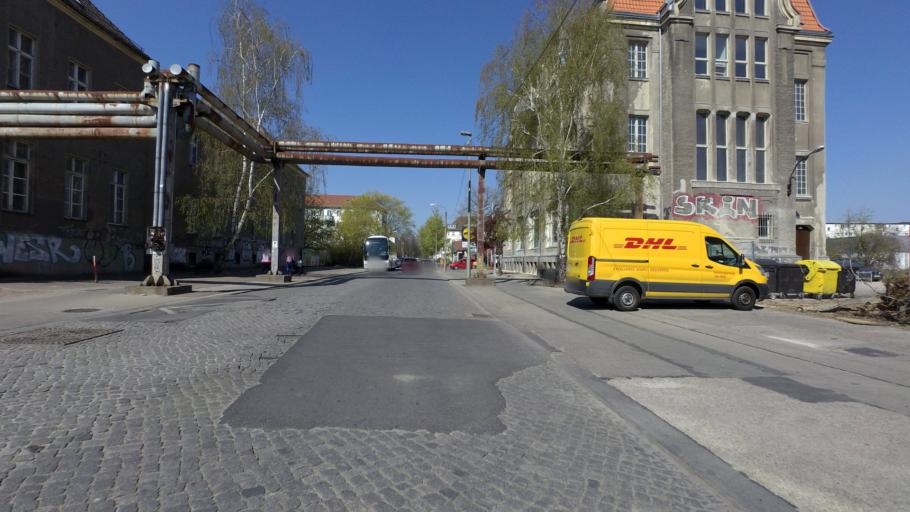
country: DE
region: Berlin
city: Alt-Hohenschoenhausen
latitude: 52.5423
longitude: 13.4989
